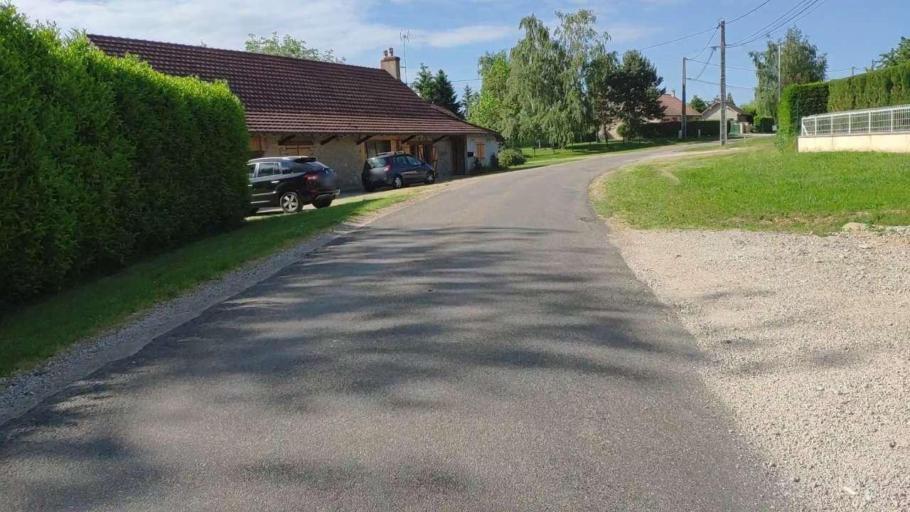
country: FR
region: Franche-Comte
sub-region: Departement du Jura
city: Bletterans
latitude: 46.7119
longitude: 5.4700
